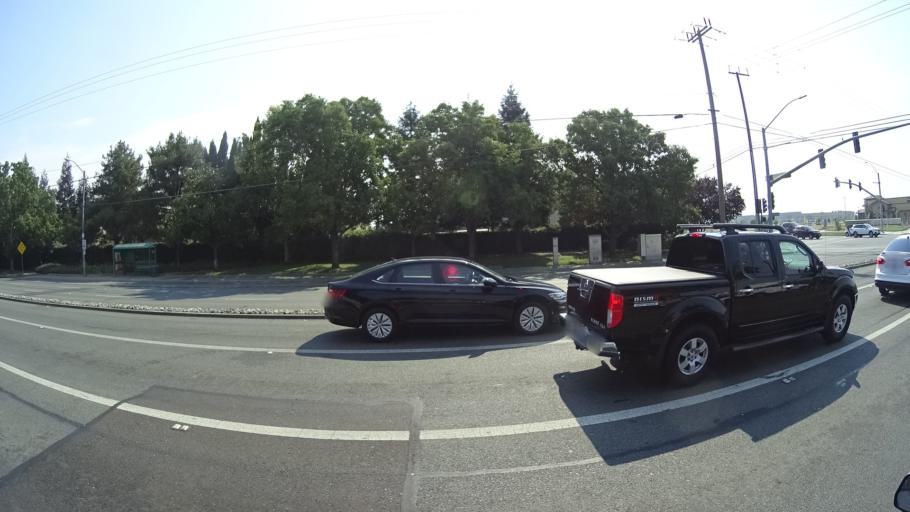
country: US
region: California
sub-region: Sacramento County
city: Laguna
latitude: 38.4095
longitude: -121.4178
